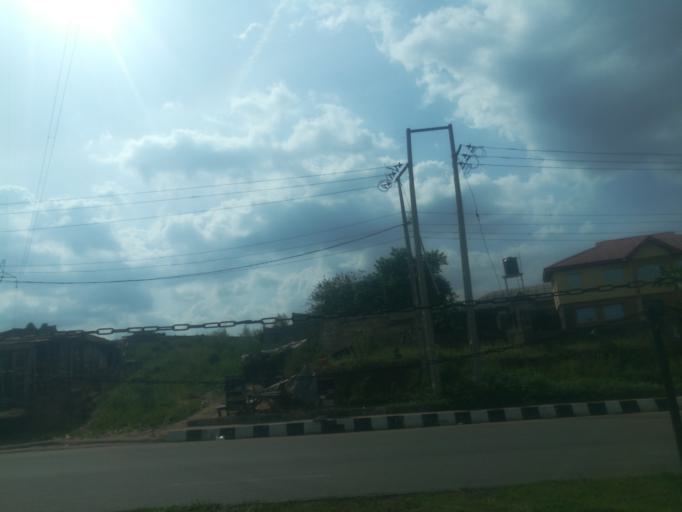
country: NG
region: Ogun
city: Abeokuta
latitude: 7.1346
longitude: 3.3661
